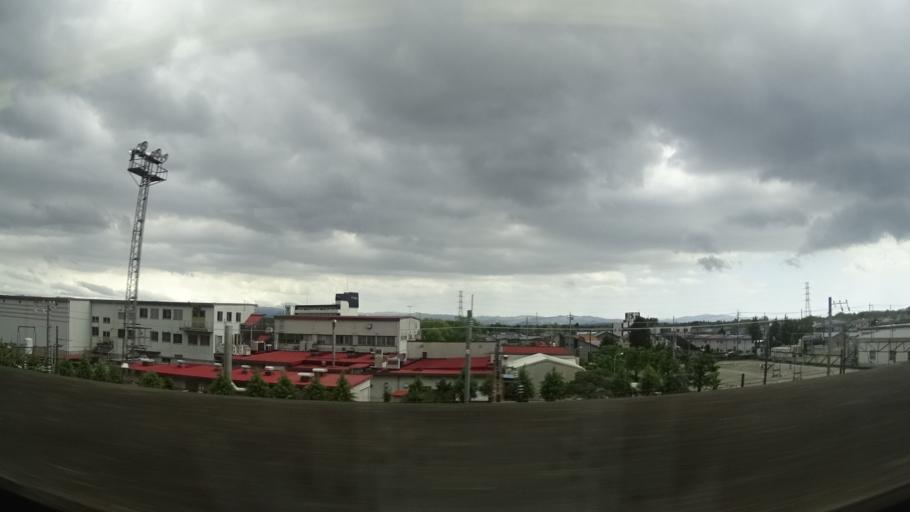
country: JP
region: Tochigi
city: Kuroiso
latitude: 36.9745
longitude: 140.0635
